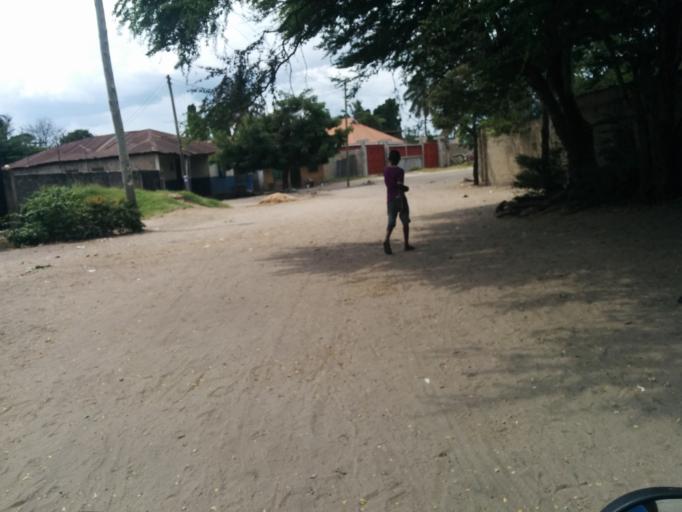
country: TZ
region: Dar es Salaam
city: Dar es Salaam
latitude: -6.8618
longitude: 39.2554
